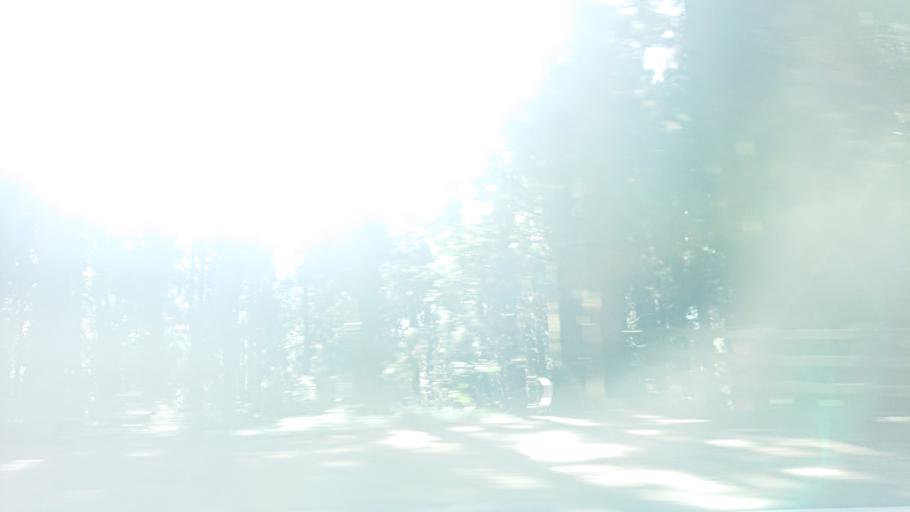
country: TW
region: Taiwan
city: Lugu
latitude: 23.5026
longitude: 120.8121
